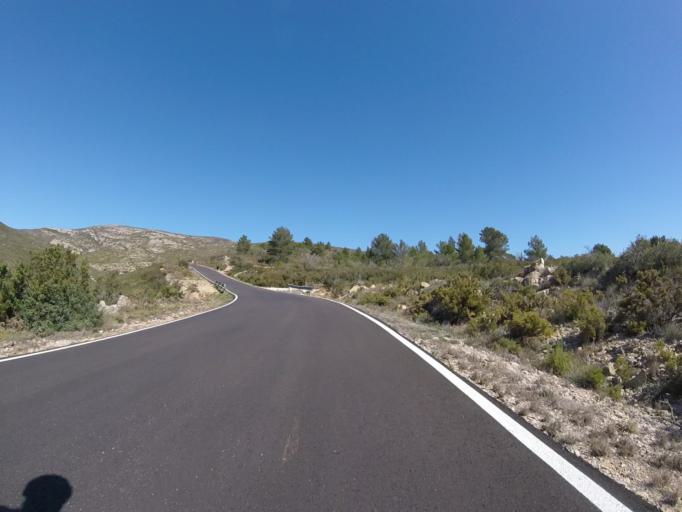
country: ES
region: Valencia
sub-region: Provincia de Castello
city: Cervera del Maestre
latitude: 40.4037
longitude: 0.2279
